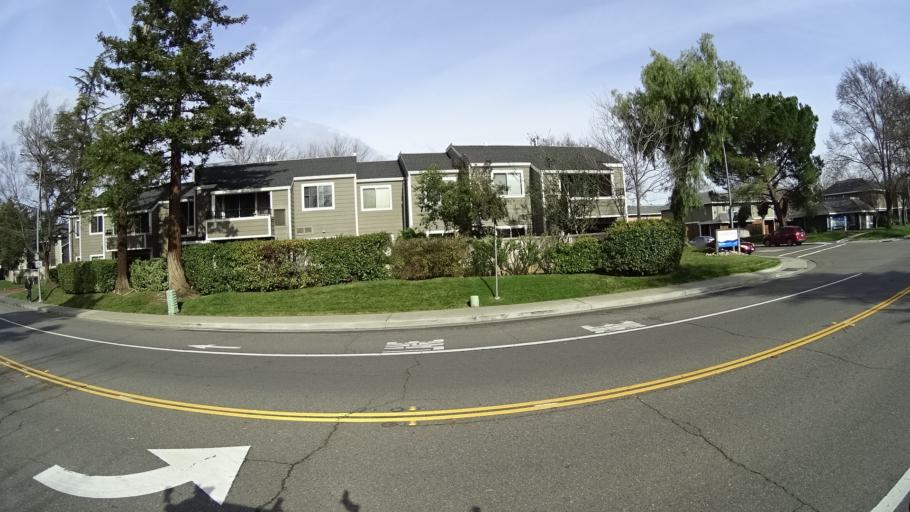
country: US
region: California
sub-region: Yolo County
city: Davis
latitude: 38.5479
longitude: -121.6999
